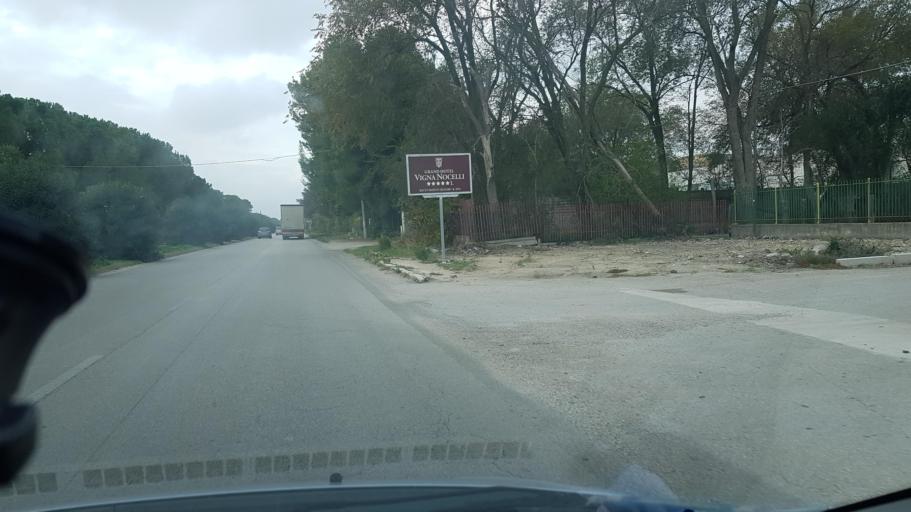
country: IT
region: Apulia
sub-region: Provincia di Foggia
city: Foggia
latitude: 41.4851
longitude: 15.5624
